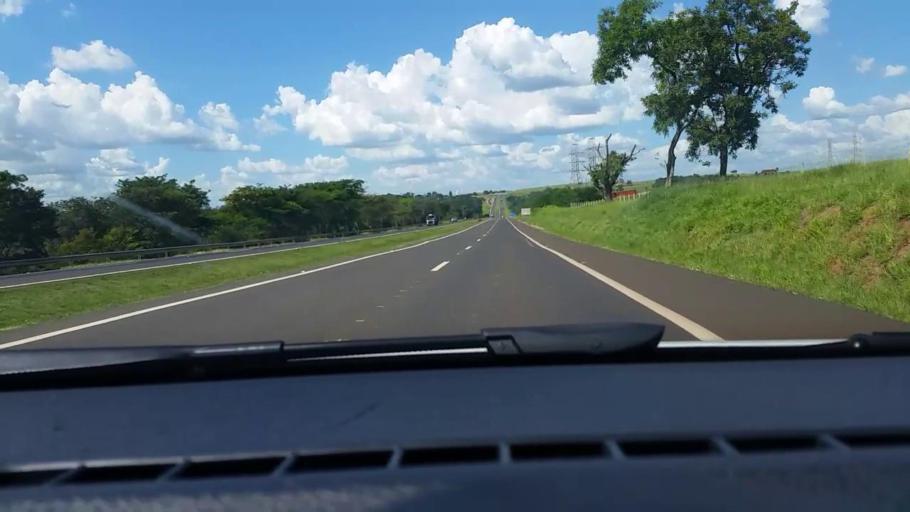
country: BR
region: Sao Paulo
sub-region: Bauru
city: Bauru
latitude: -22.4134
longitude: -49.1051
